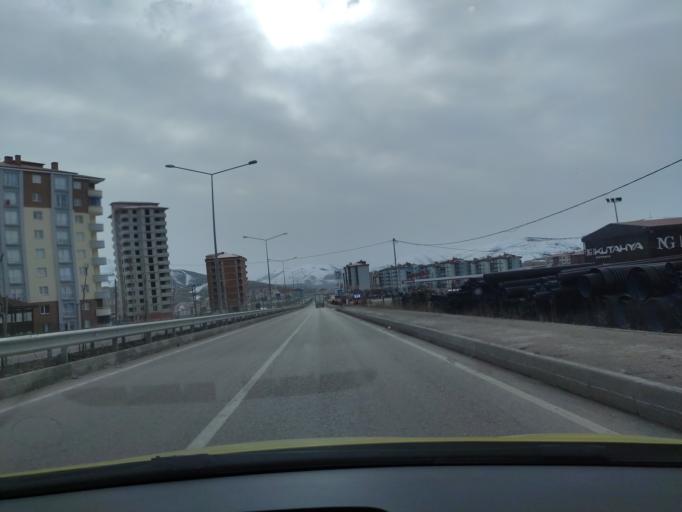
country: TR
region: Bayburt
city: Bayburt
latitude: 40.2701
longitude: 40.1964
